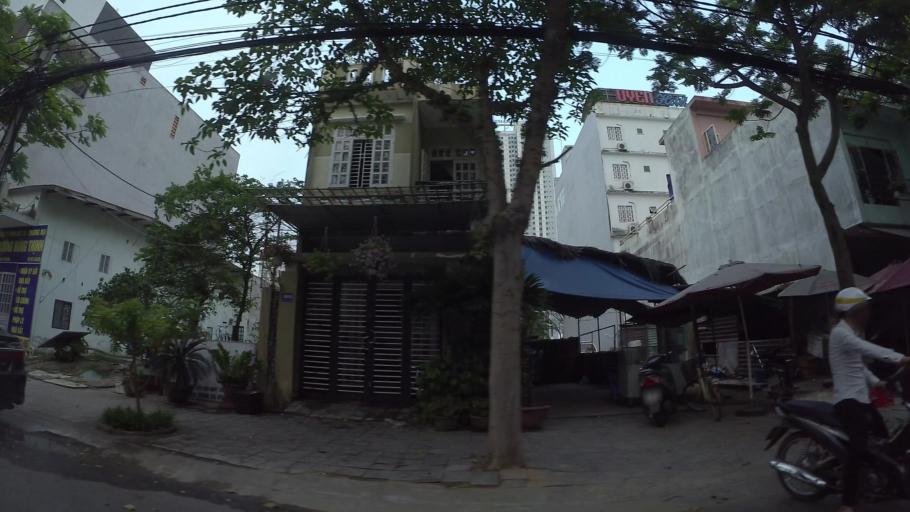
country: VN
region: Da Nang
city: Son Tra
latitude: 16.0527
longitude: 108.2448
